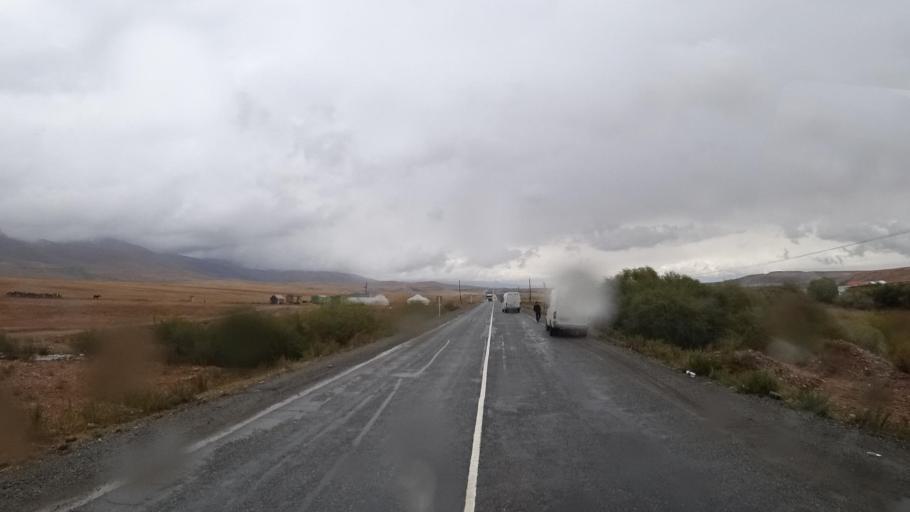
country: KG
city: Sosnovka
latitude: 42.2199
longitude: 73.6971
